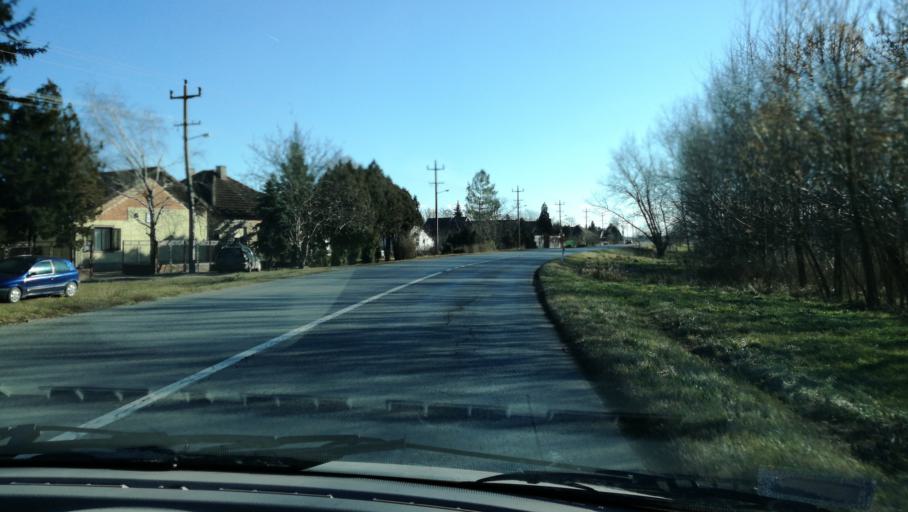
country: HU
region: Csongrad
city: Asotthalom
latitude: 46.1119
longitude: 19.8406
